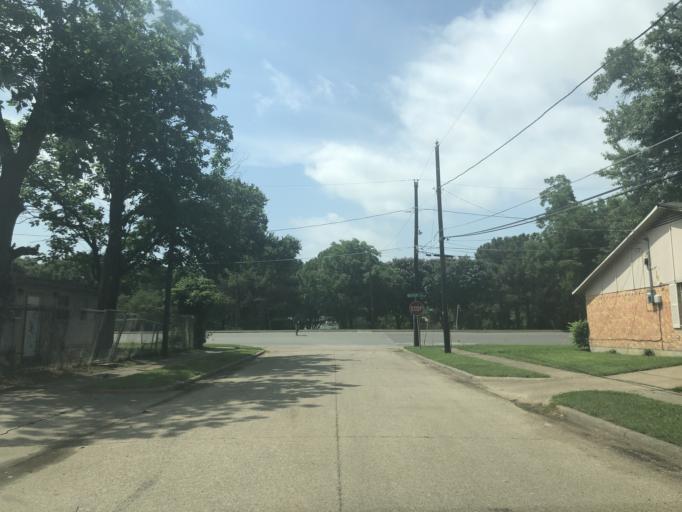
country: US
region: Texas
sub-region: Dallas County
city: Cockrell Hill
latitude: 32.7900
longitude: -96.8812
